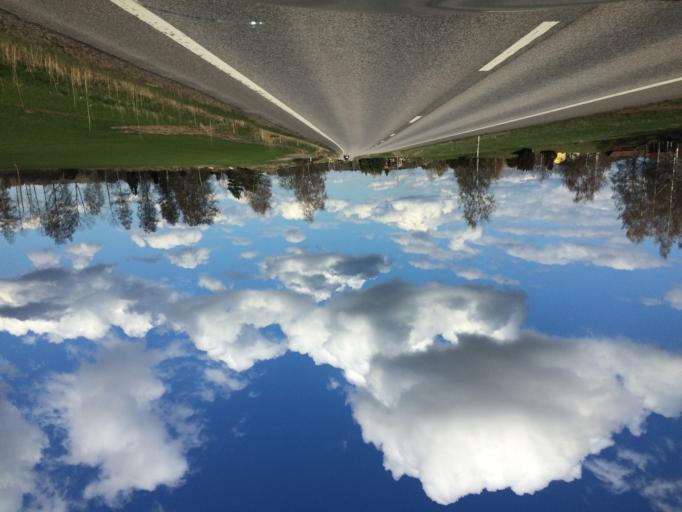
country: SE
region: Soedermanland
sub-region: Eskilstuna Kommun
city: Eskilstuna
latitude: 59.4009
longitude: 16.5611
